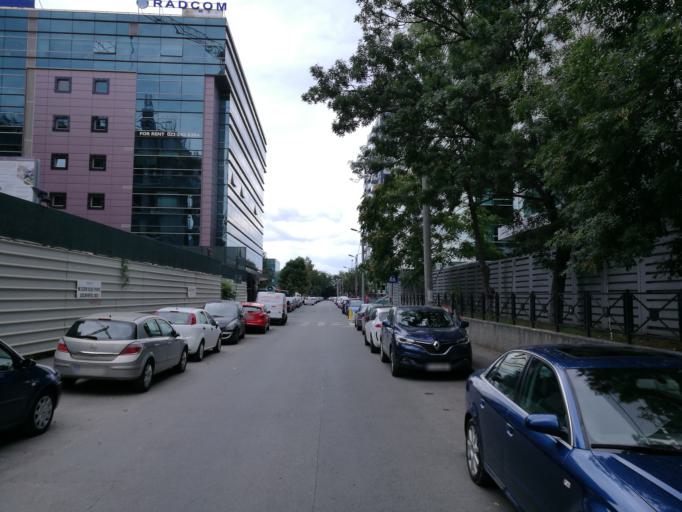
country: RO
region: Bucuresti
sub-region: Municipiul Bucuresti
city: Bucharest
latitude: 44.4799
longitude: 26.1156
